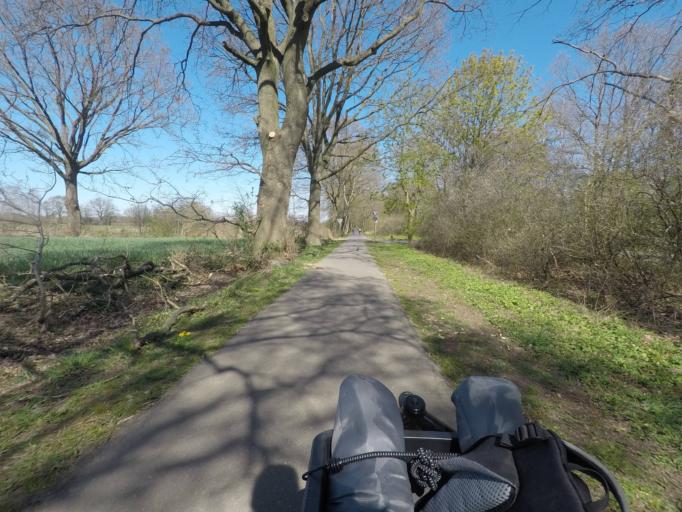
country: DE
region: Schleswig-Holstein
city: Braak
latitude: 53.5989
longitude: 10.2727
